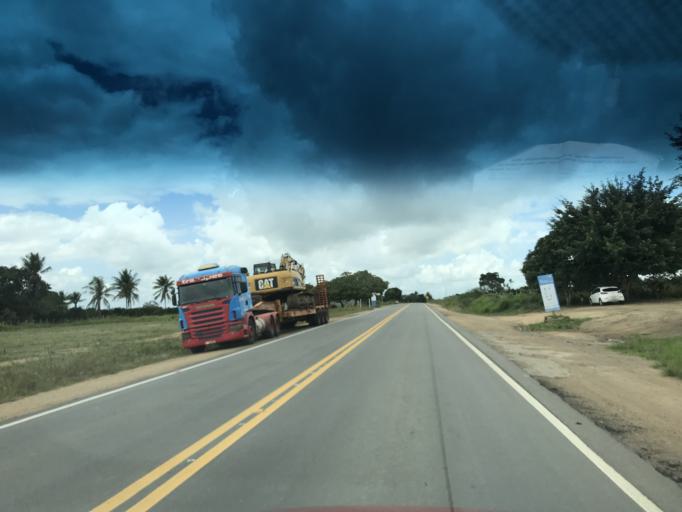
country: BR
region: Bahia
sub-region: Conceicao Do Almeida
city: Conceicao do Almeida
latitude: -12.6936
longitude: -39.2449
